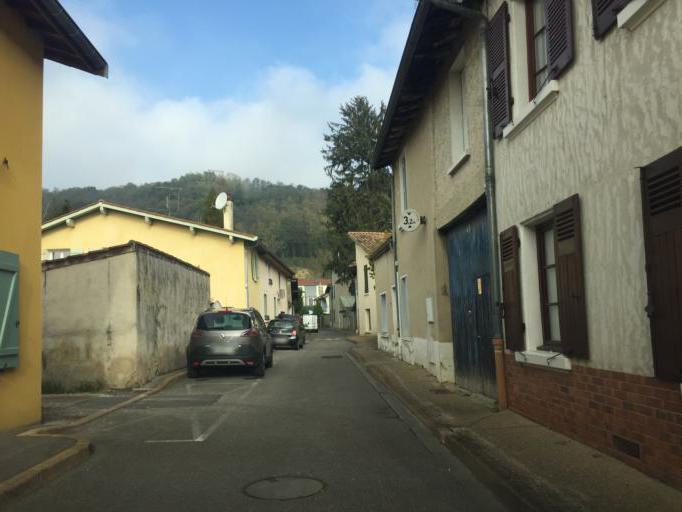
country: FR
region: Rhone-Alpes
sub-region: Departement de l'Ain
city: Miribel
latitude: 45.8289
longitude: 4.9637
